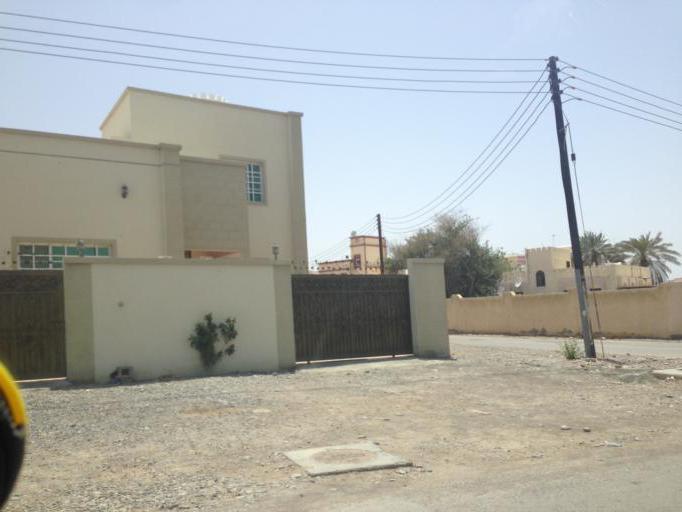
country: OM
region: Muhafazat Masqat
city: As Sib al Jadidah
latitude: 23.6820
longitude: 58.1221
